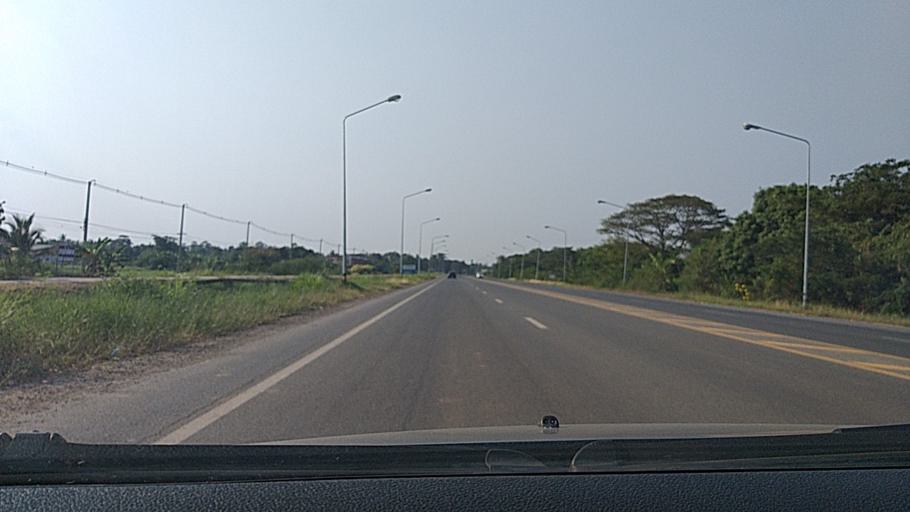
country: TH
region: Sing Buri
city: Sing Buri
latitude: 14.8578
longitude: 100.4093
